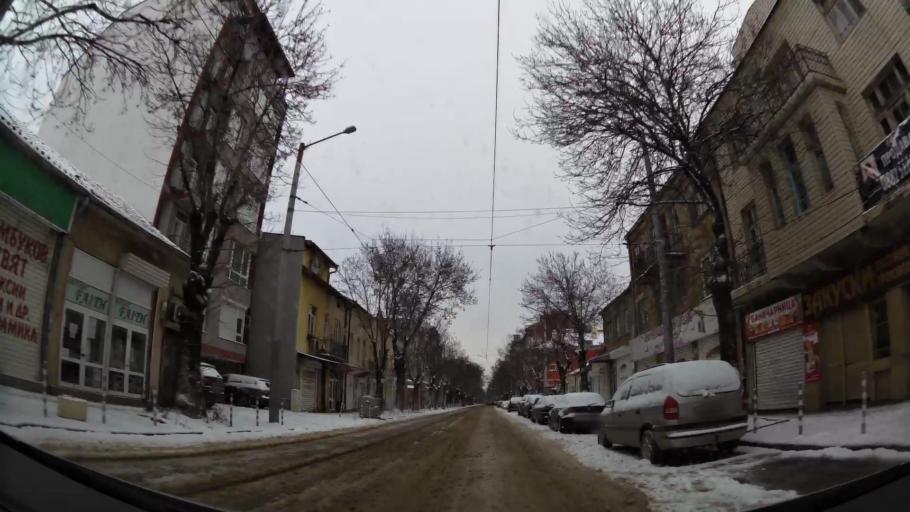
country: BG
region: Sofia-Capital
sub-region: Stolichna Obshtina
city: Sofia
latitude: 42.7019
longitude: 23.3060
